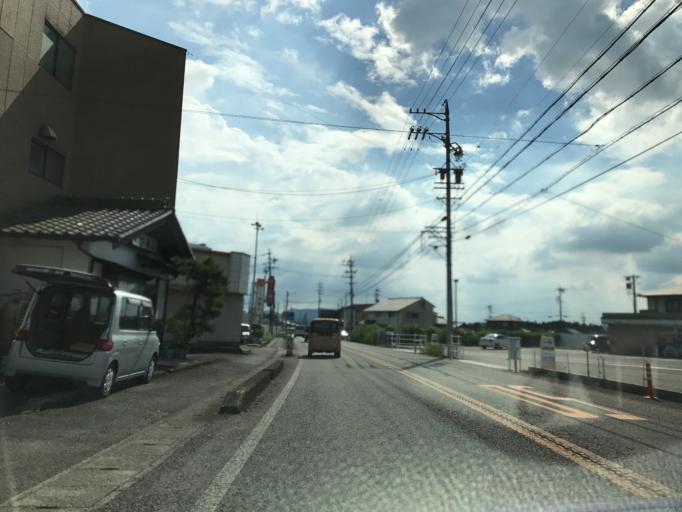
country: JP
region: Gifu
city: Mino
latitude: 35.4889
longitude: 136.8729
